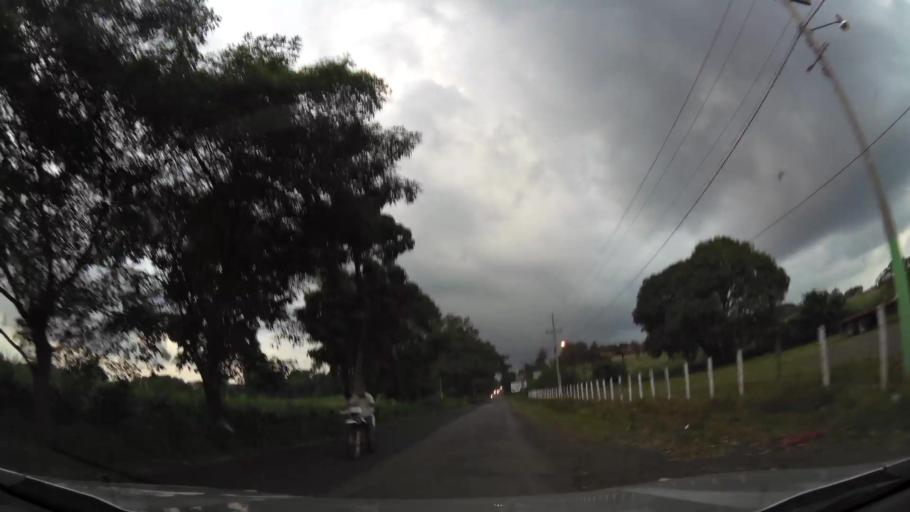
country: GT
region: Escuintla
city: Santa Lucia Cotzumalguapa
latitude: 14.3128
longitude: -91.0427
